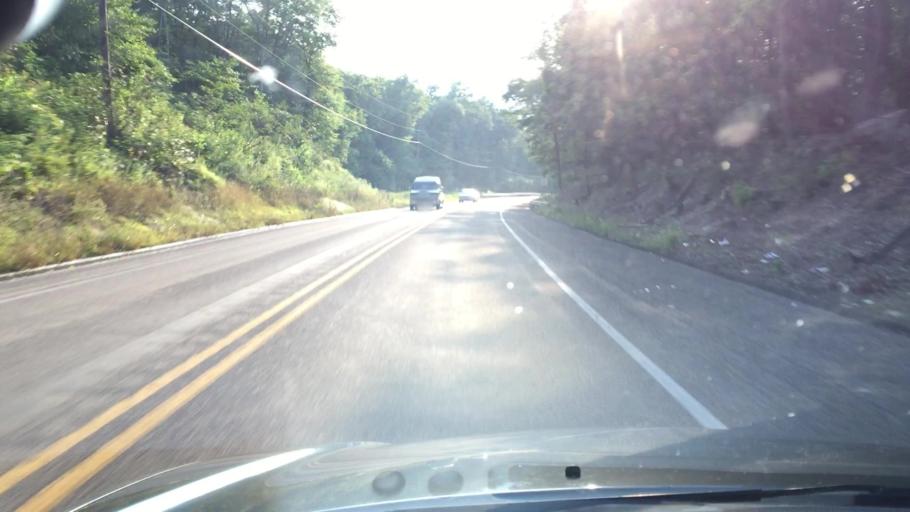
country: US
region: Pennsylvania
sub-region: Carbon County
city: Weatherly
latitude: 40.9121
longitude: -75.8439
